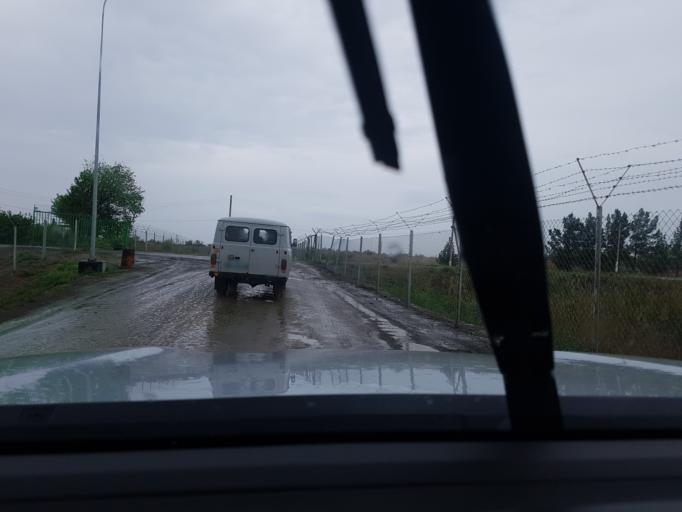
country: TM
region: Lebap
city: Farap
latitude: 39.2168
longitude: 63.7171
